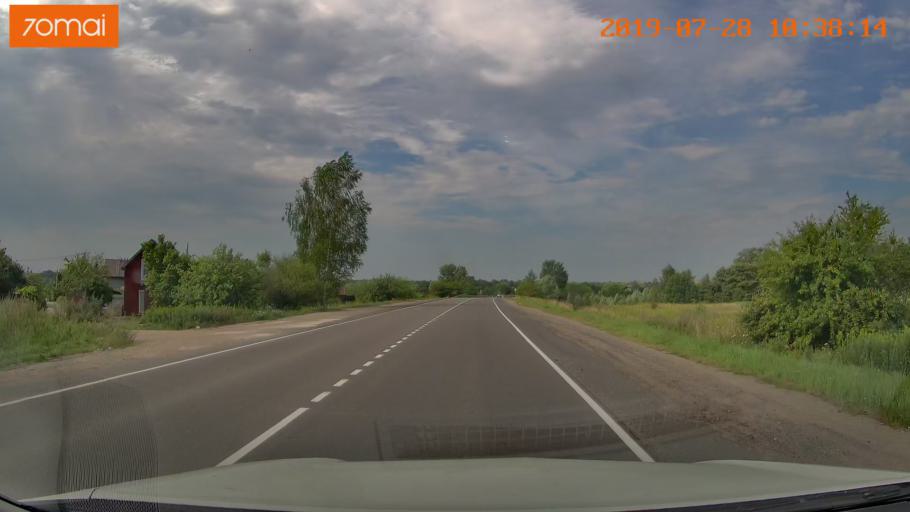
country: RU
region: Kaliningrad
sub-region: Gorod Kaliningrad
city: Kaliningrad
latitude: 54.7254
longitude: 20.4020
